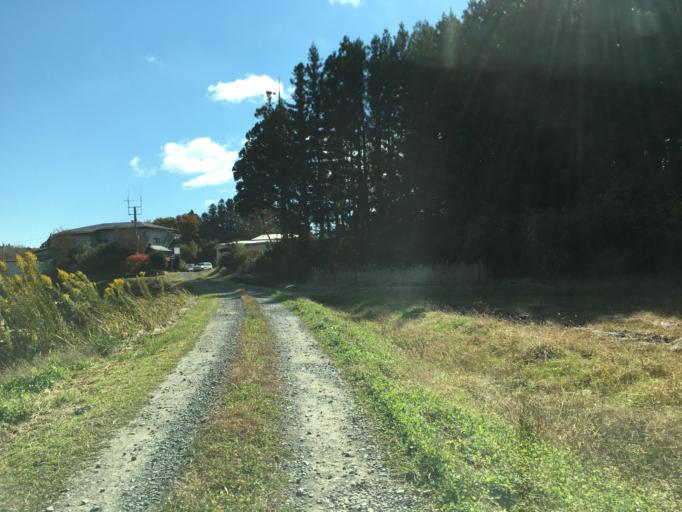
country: JP
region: Fukushima
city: Ishikawa
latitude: 37.2406
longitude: 140.5622
